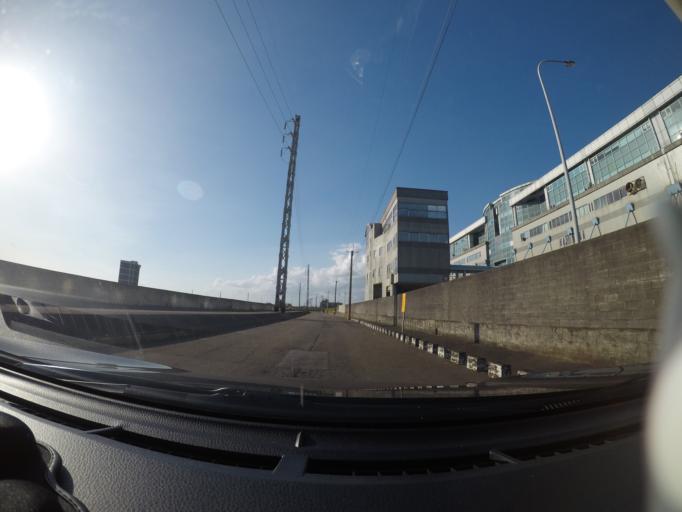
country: TW
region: Taiwan
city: Taoyuan City
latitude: 25.1076
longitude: 121.2502
